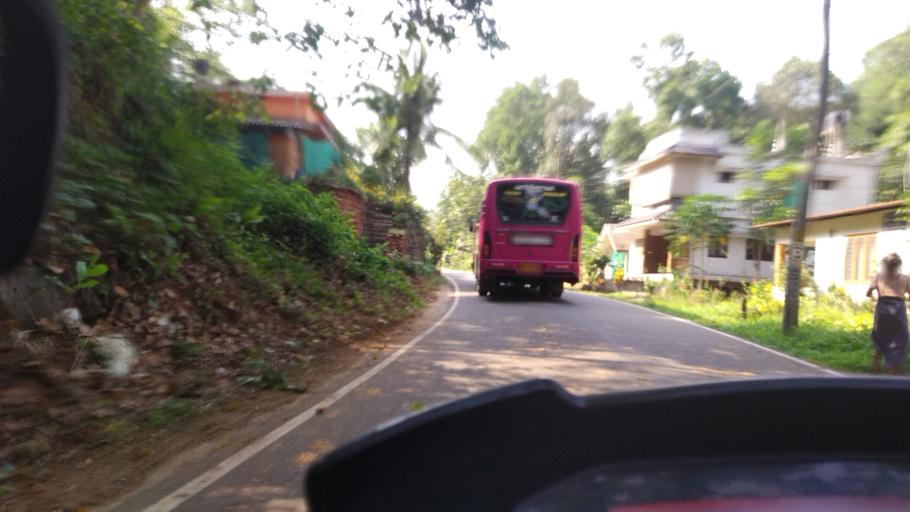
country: IN
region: Kerala
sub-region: Ernakulam
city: Piravam
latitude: 9.8167
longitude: 76.5578
